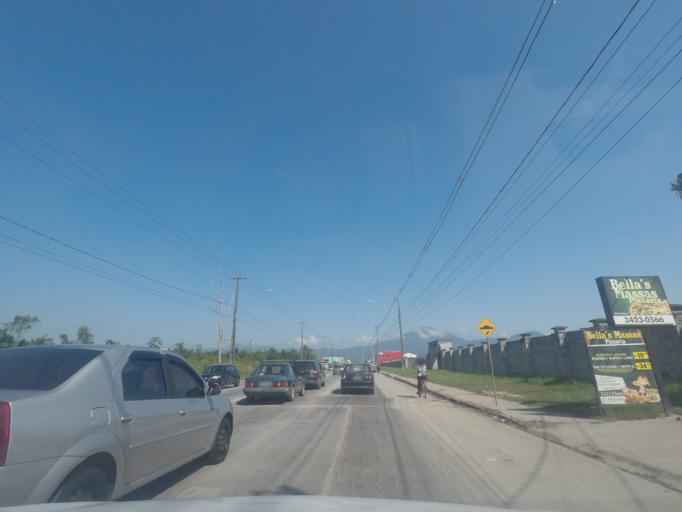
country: BR
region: Parana
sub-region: Paranagua
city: Paranagua
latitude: -25.5610
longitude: -48.5622
